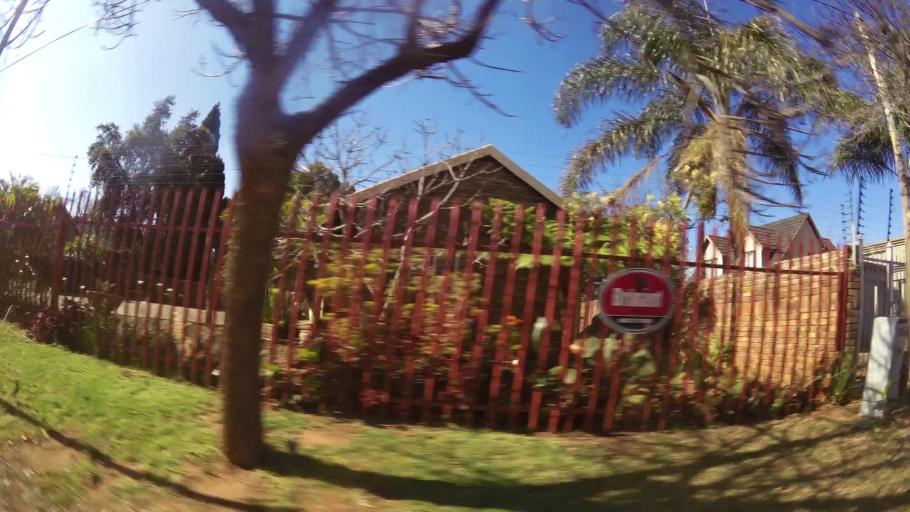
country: ZA
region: Gauteng
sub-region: City of Tshwane Metropolitan Municipality
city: Centurion
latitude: -25.8308
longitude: 28.2403
